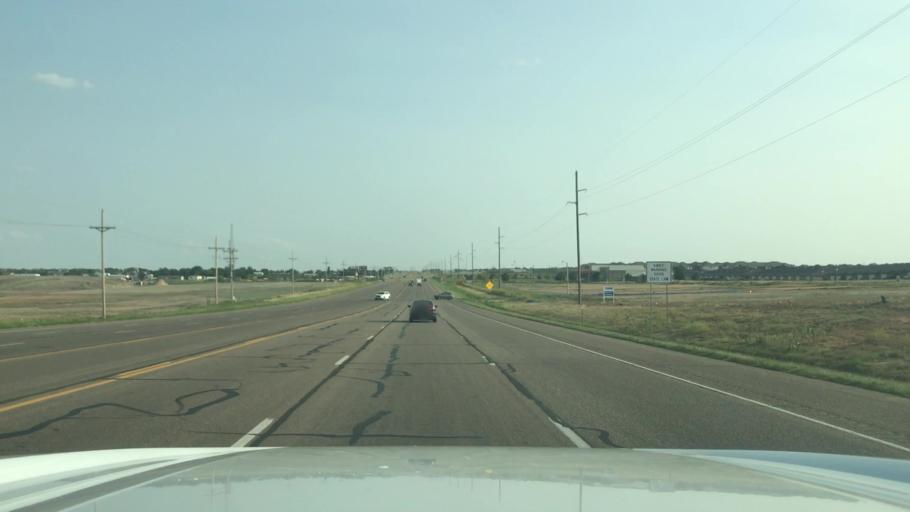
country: US
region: Texas
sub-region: Potter County
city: Amarillo
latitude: 35.1385
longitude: -101.9382
